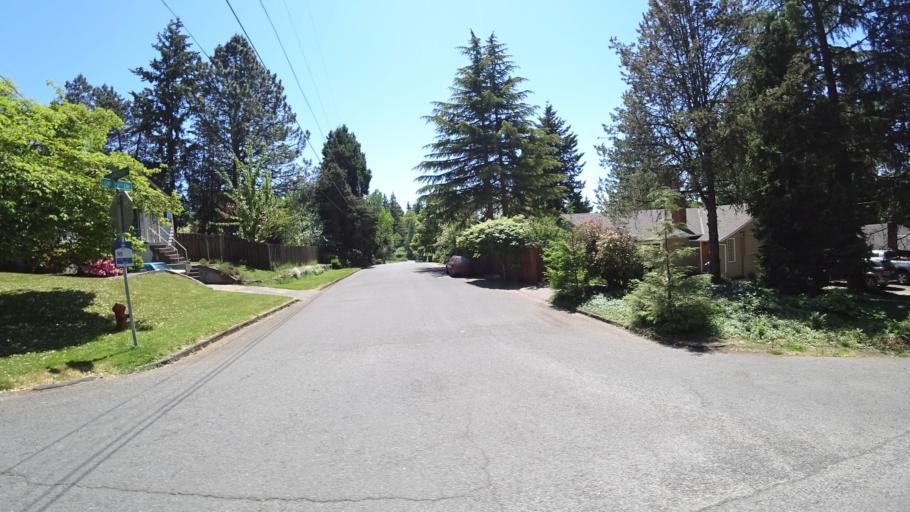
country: US
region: Oregon
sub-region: Washington County
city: Raleigh Hills
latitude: 45.4907
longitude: -122.7167
